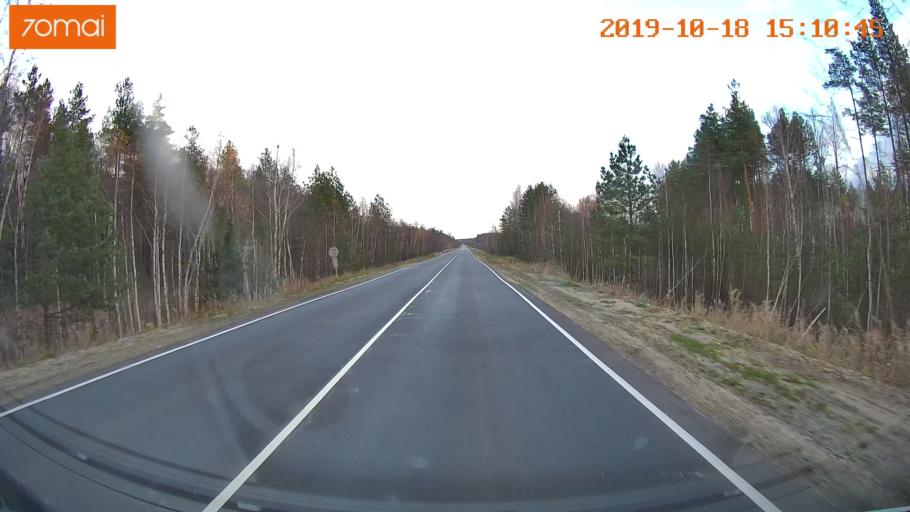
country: RU
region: Vladimir
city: Gus'-Khrustal'nyy
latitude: 55.5690
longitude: 40.6522
